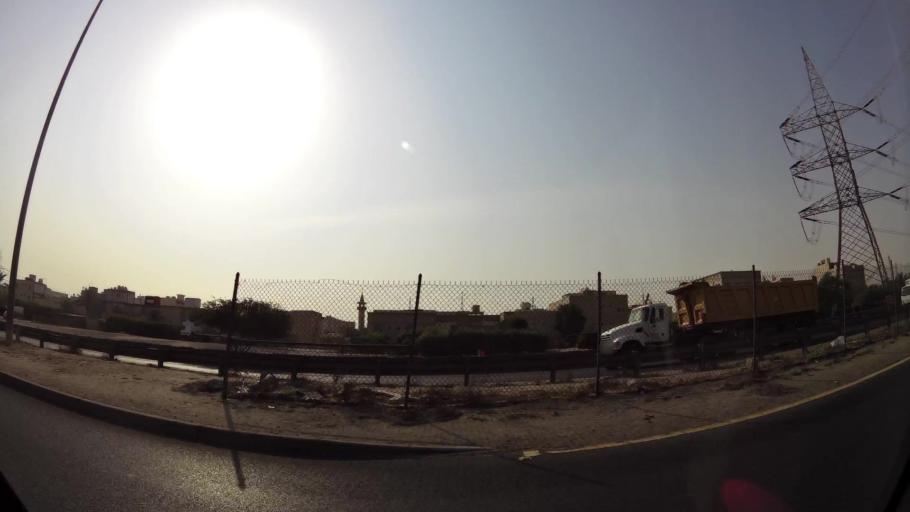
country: KW
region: Mubarak al Kabir
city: Mubarak al Kabir
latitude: 29.1745
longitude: 48.0636
